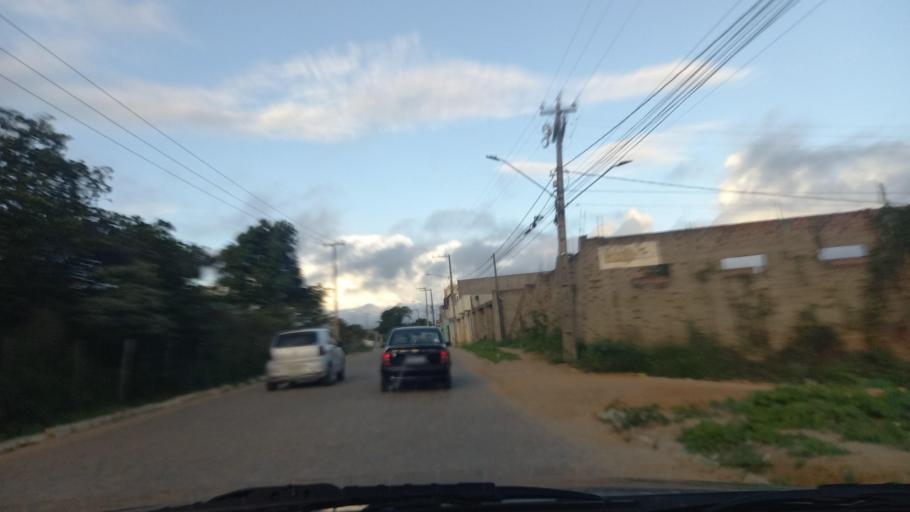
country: BR
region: Pernambuco
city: Garanhuns
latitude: -8.8907
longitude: -36.4517
